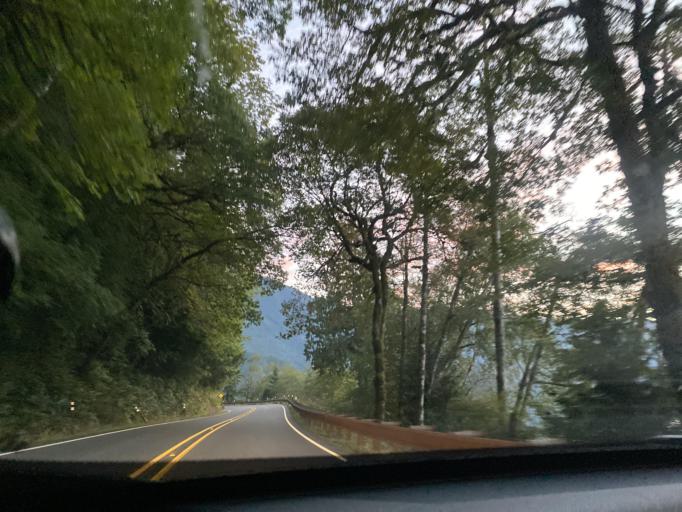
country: CA
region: British Columbia
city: Sooke
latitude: 48.0685
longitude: -123.7752
